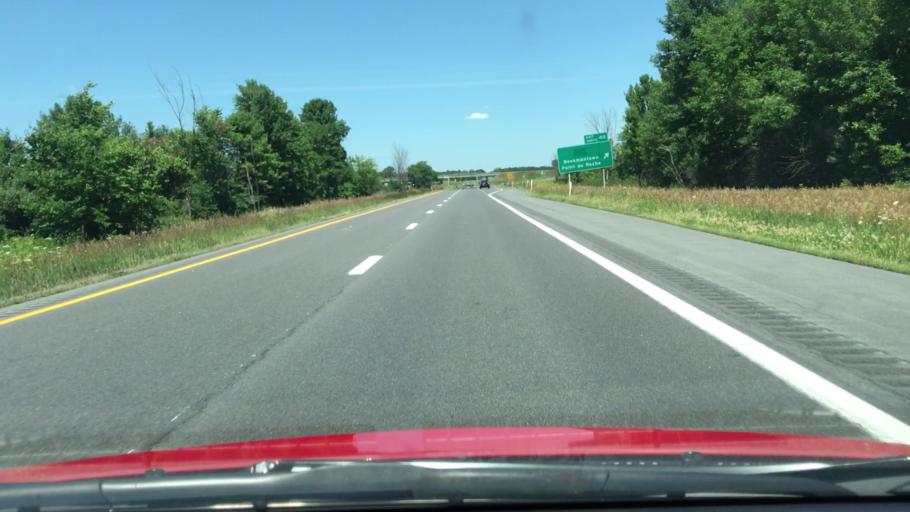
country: US
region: New York
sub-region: Clinton County
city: Cumberland Head
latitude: 44.7765
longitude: -73.4355
